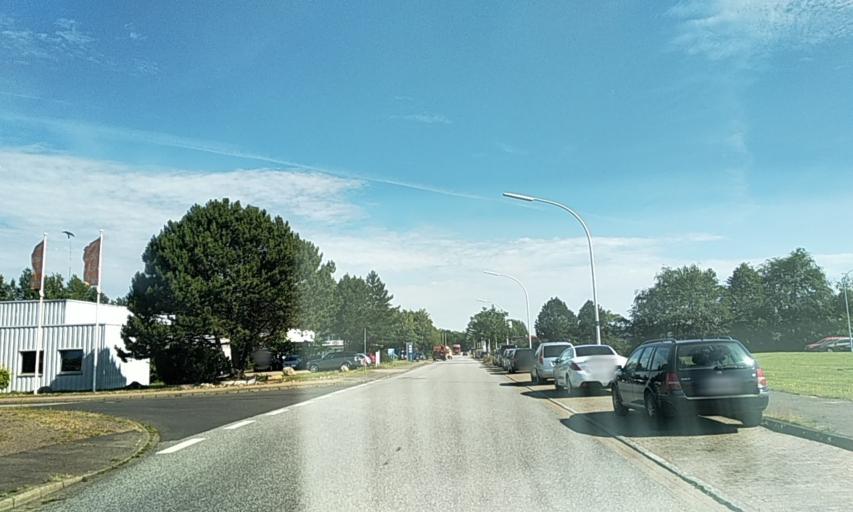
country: DE
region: Schleswig-Holstein
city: Fockbek
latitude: 54.3187
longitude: 9.6169
